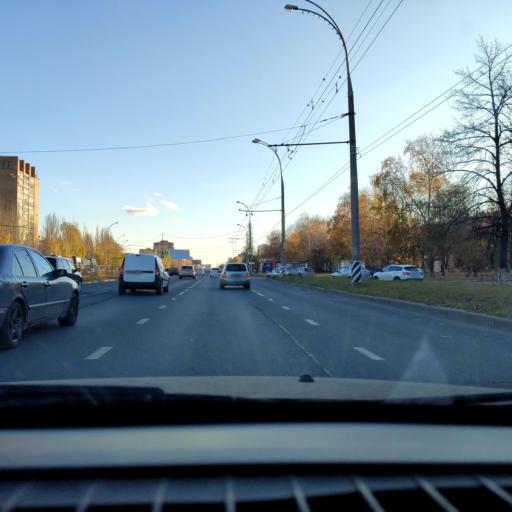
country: RU
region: Samara
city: Tol'yatti
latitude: 53.5228
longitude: 49.2957
